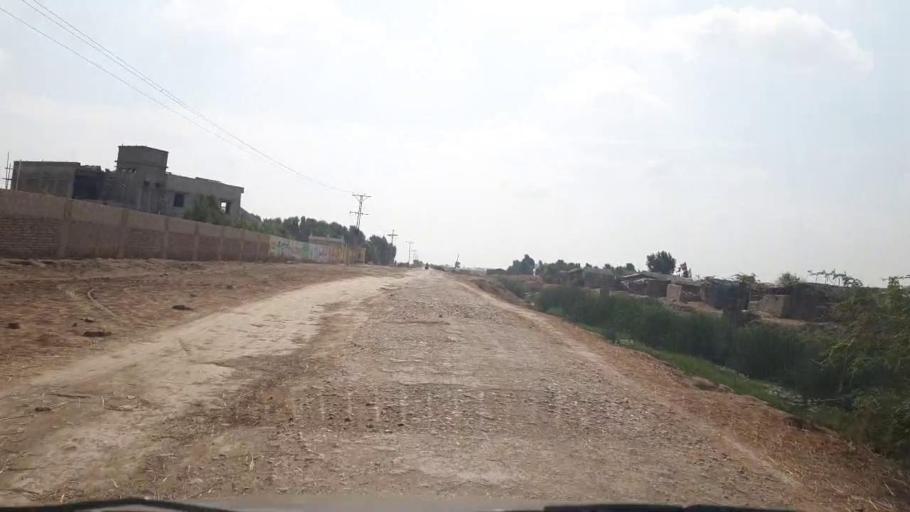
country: PK
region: Sindh
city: Kario
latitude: 24.6375
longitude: 68.5472
